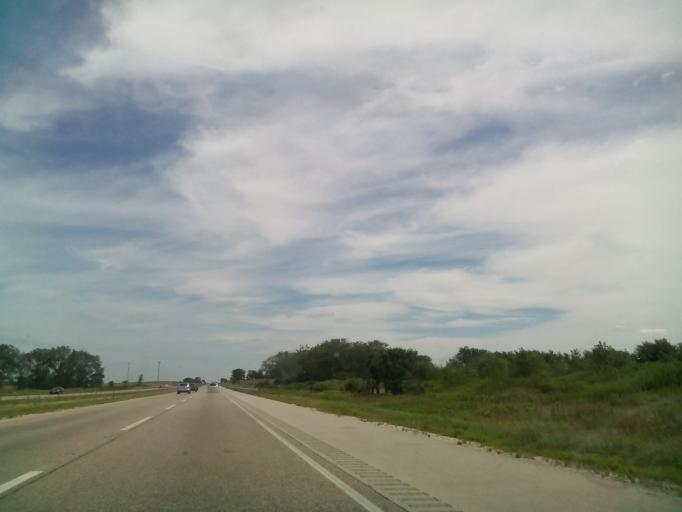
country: US
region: Illinois
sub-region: DeKalb County
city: Cortland
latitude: 41.9007
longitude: -88.6750
